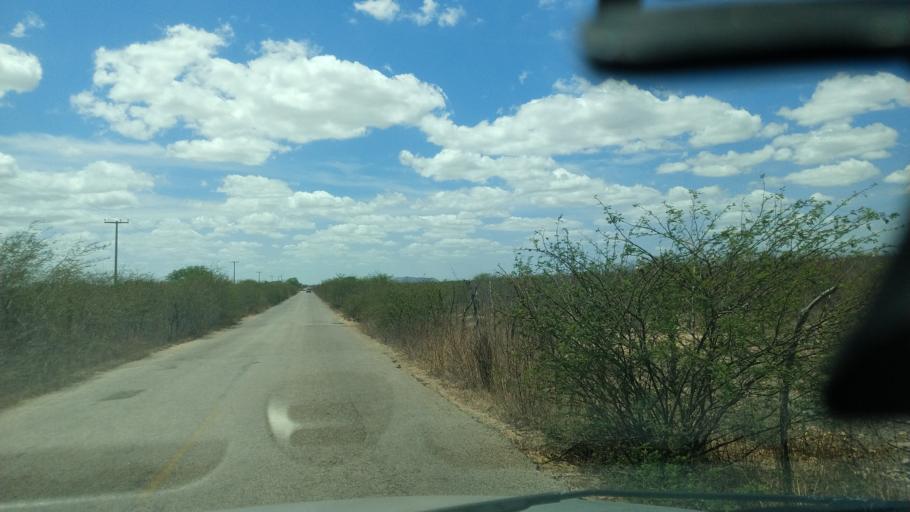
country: BR
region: Rio Grande do Norte
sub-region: Sao Paulo Do Potengi
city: Sao Paulo do Potengi
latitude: -5.9151
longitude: -35.7594
